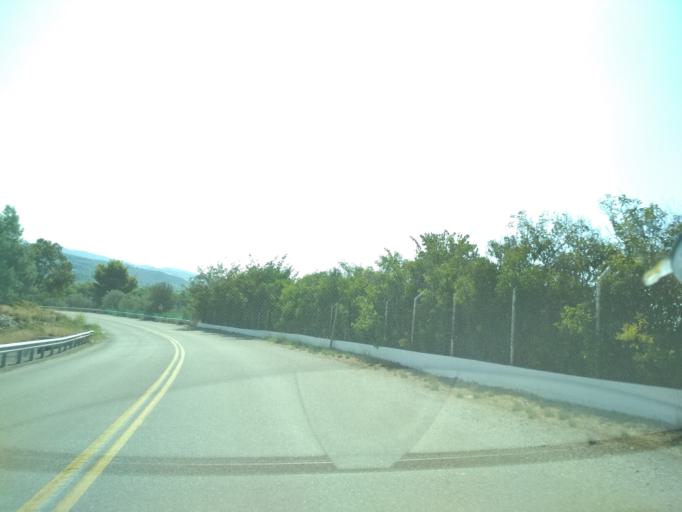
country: GR
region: Central Greece
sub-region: Nomos Evvoias
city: Roviai
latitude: 38.8315
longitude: 23.2009
